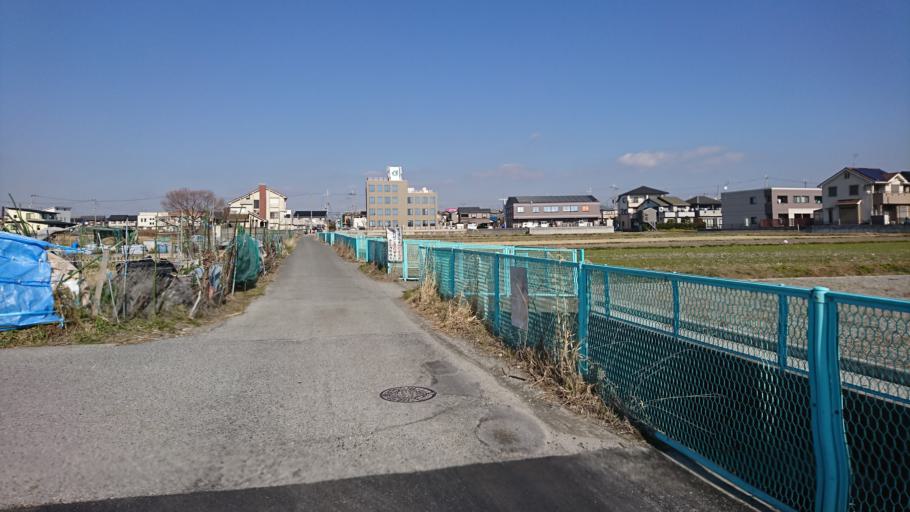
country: JP
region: Hyogo
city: Kakogawacho-honmachi
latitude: 34.7425
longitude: 134.8539
